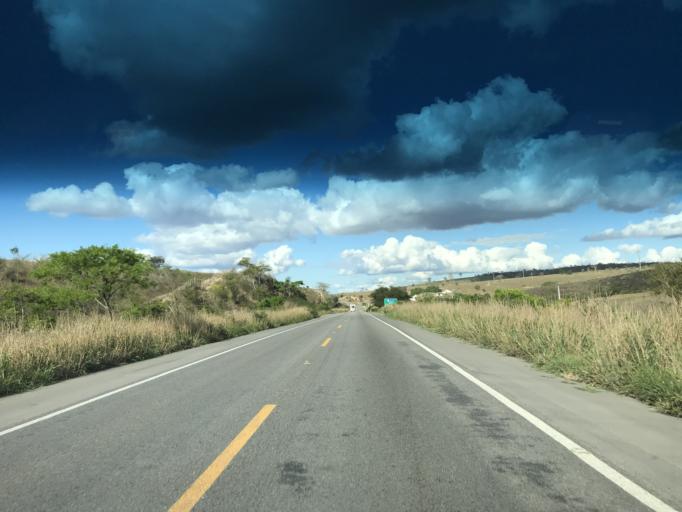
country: BR
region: Bahia
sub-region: Andarai
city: Vera Cruz
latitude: -12.4631
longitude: -40.9015
